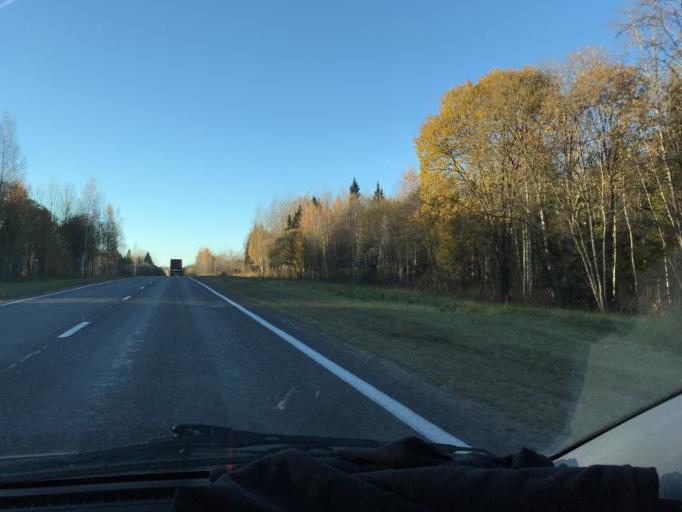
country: BY
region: Vitebsk
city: Vitebsk
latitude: 55.3476
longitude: 30.2118
